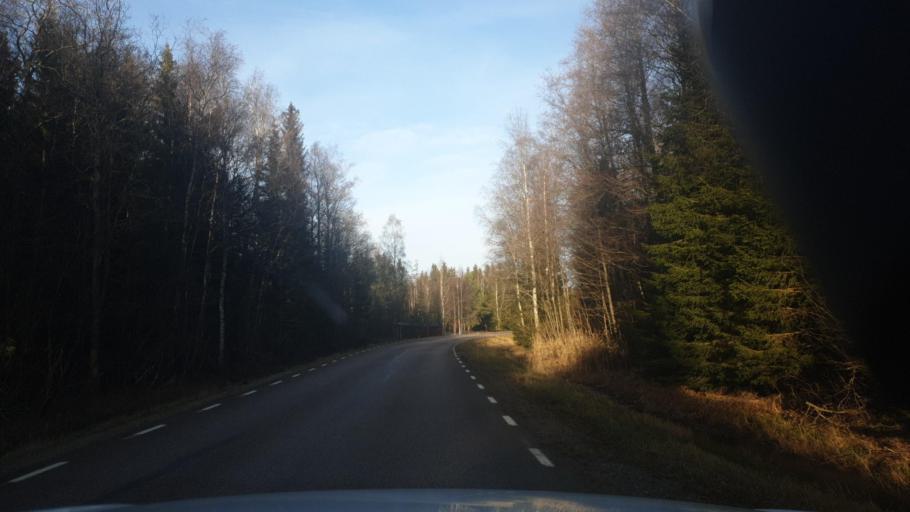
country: SE
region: Vaermland
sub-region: Grums Kommun
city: Slottsbron
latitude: 59.4846
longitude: 12.8825
